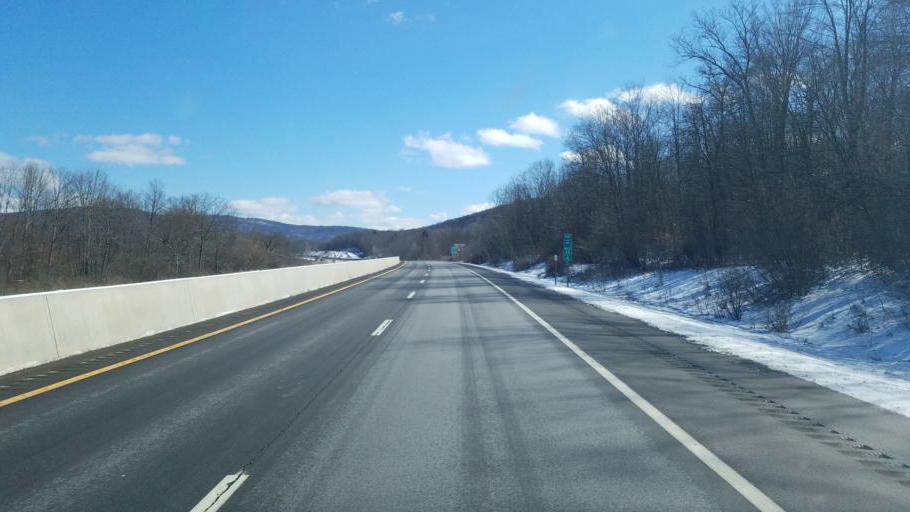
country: US
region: New York
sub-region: Cattaraugus County
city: Salamanca
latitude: 42.1028
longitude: -78.6617
